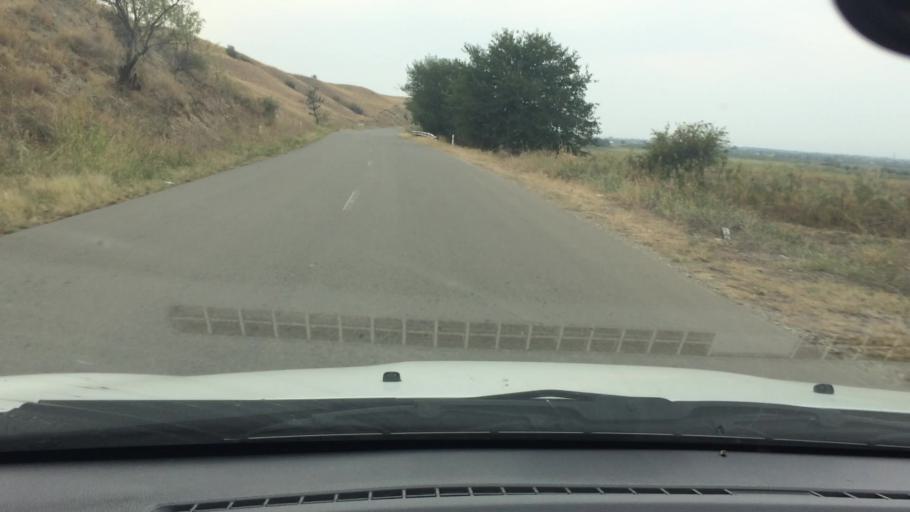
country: AM
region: Tavush
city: Berdavan
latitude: 41.3381
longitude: 45.0020
